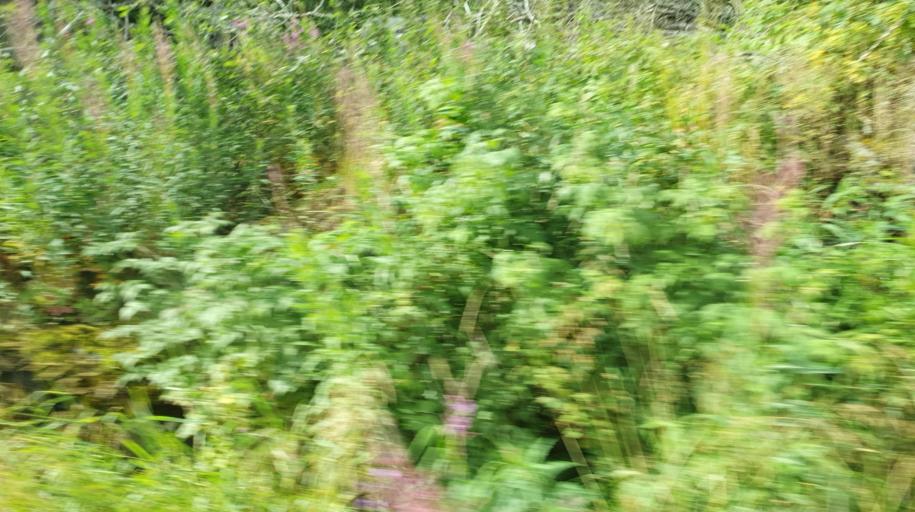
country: NO
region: Nord-Trondelag
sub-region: Levanger
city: Skogn
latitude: 63.5972
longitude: 11.2689
